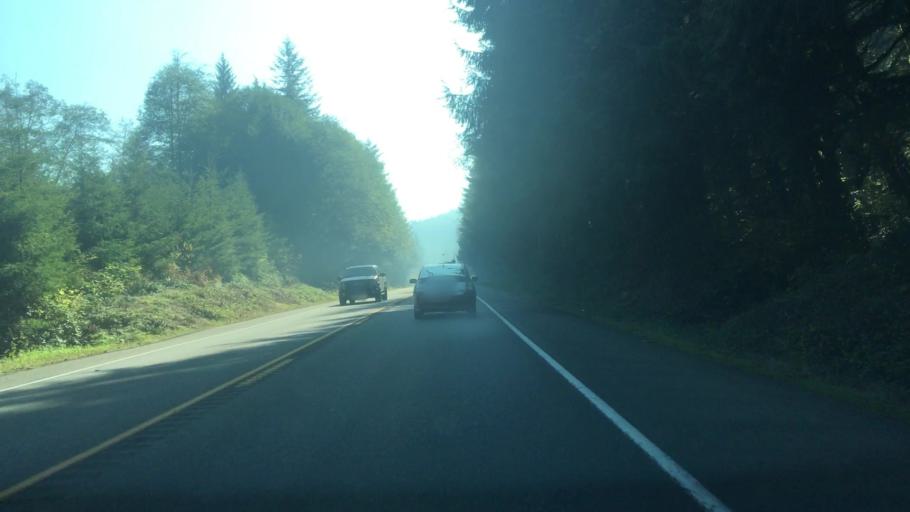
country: US
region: Washington
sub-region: Grays Harbor County
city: Central Park
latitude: 46.9256
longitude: -123.7167
